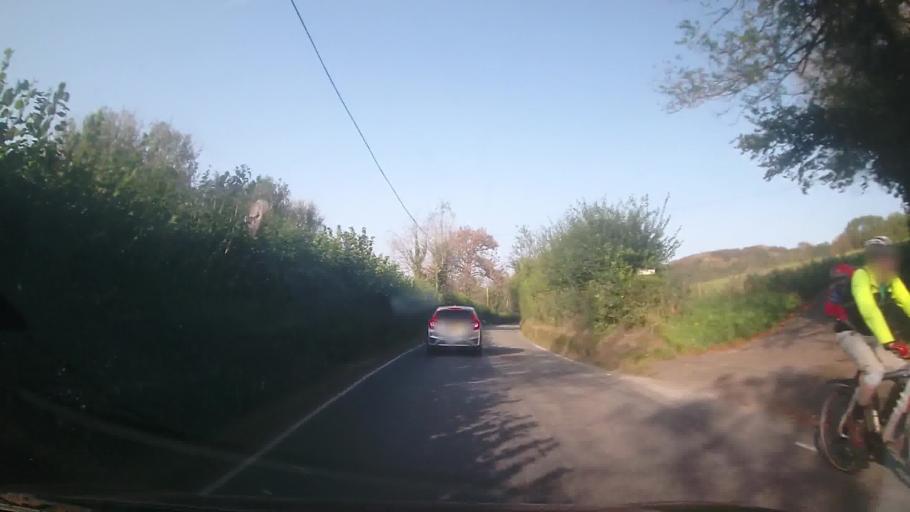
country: GB
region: Wales
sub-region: County of Ceredigion
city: Lledrod
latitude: 52.2426
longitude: -3.9203
